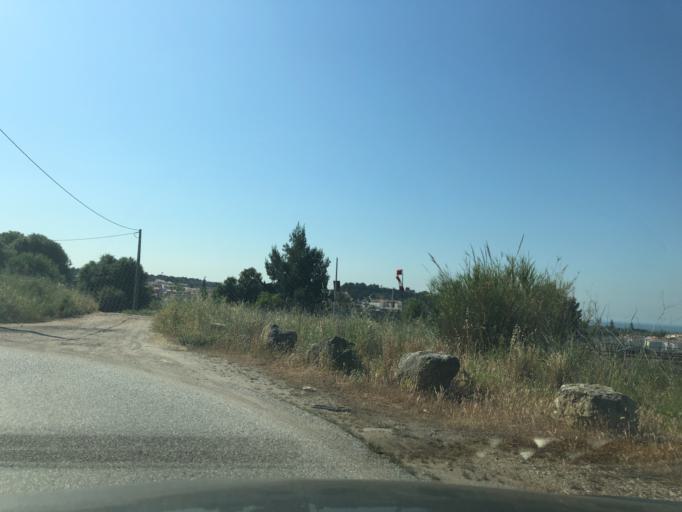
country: PT
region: Lisbon
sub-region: Oeiras
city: Quejas
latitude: 38.7166
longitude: -9.2741
